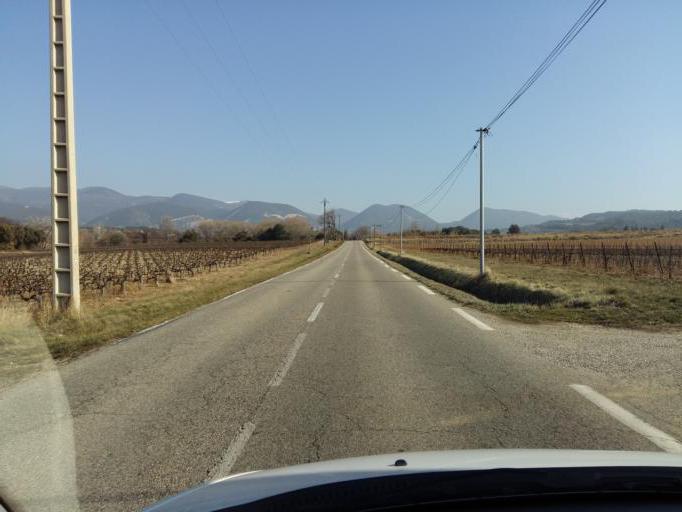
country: FR
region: Provence-Alpes-Cote d'Azur
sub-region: Departement du Vaucluse
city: Valreas
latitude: 44.3905
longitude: 5.0234
